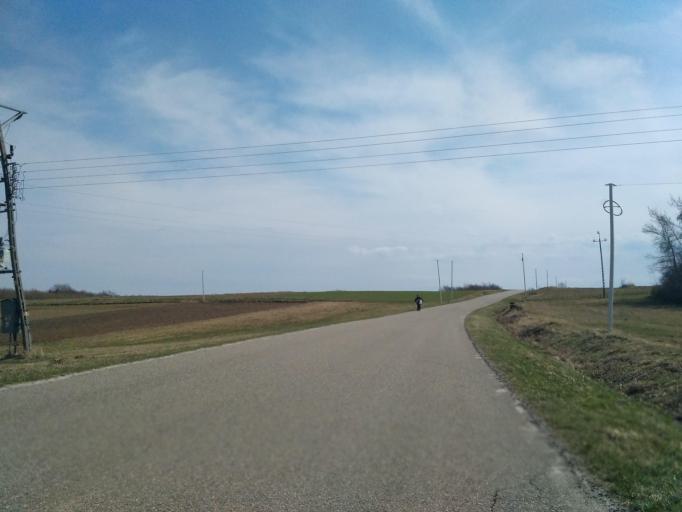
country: PL
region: Subcarpathian Voivodeship
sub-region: Powiat ropczycko-sedziszowski
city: Iwierzyce
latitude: 49.9812
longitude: 21.7417
